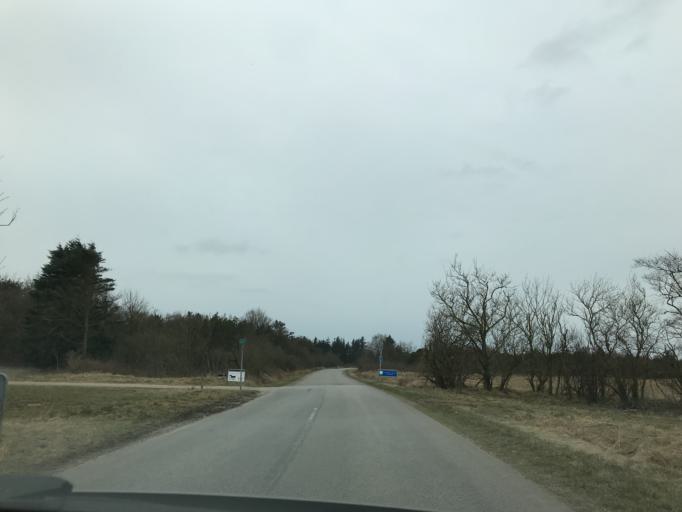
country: DK
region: South Denmark
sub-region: Varde Kommune
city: Oksbol
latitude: 55.8046
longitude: 8.3301
